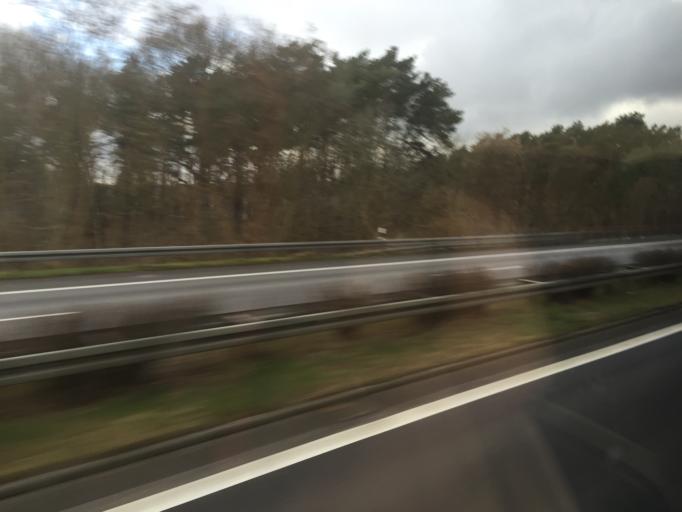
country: DE
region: Berlin
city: Blankenfelde
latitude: 52.6721
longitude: 13.4011
